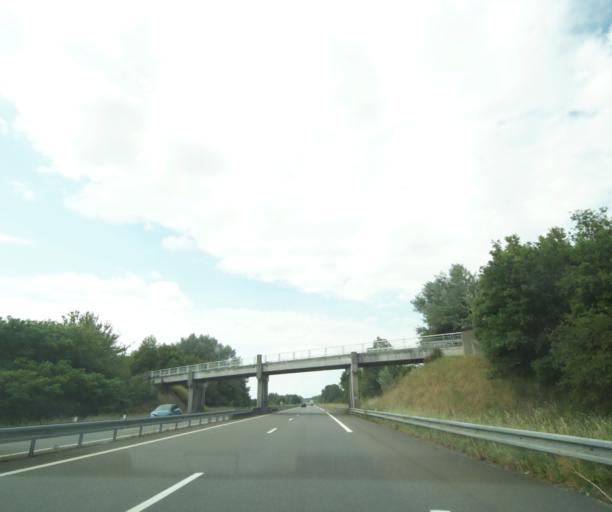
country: FR
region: Pays de la Loire
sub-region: Departement de Maine-et-Loire
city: Brion
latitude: 47.4542
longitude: -0.1786
